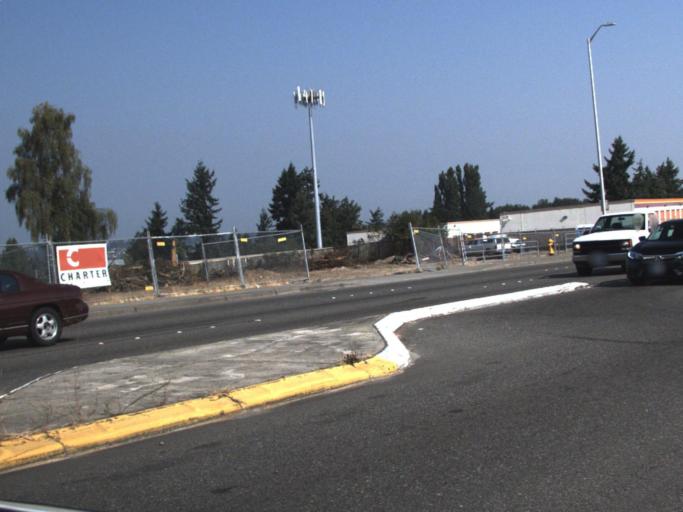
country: US
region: Washington
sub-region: King County
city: Des Moines
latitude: 47.3895
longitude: -122.2956
